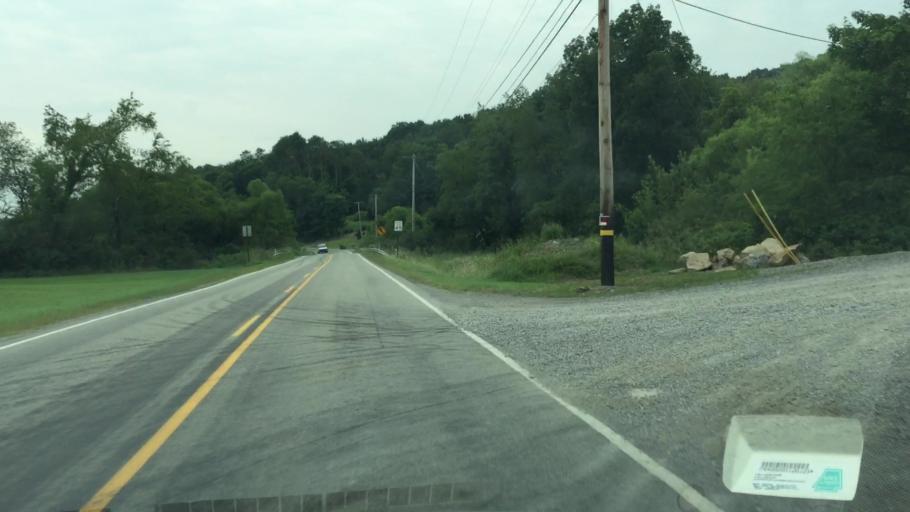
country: US
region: Pennsylvania
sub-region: Allegheny County
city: Curtisville
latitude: 40.6927
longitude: -79.8391
